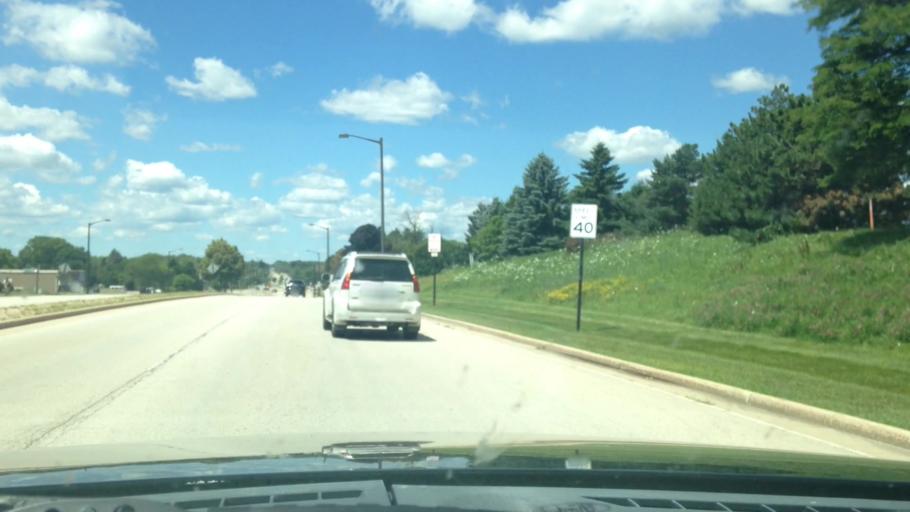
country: US
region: Wisconsin
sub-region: Waukesha County
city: Butler
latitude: 43.1483
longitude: -88.0686
